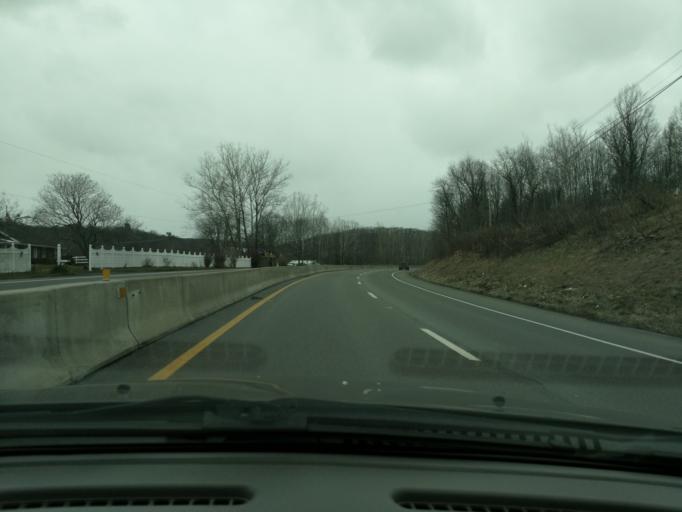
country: US
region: Pennsylvania
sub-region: Berks County
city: West Hamburg
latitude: 40.6028
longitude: -76.0280
